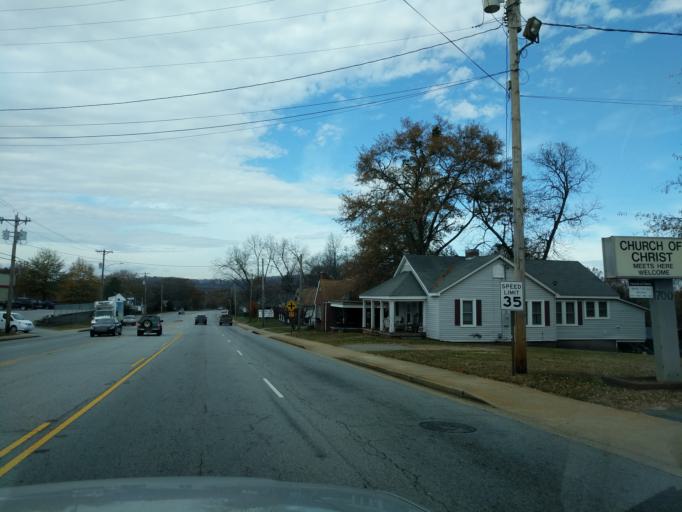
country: US
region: South Carolina
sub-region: Pickens County
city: Easley
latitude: 34.8304
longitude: -82.6152
